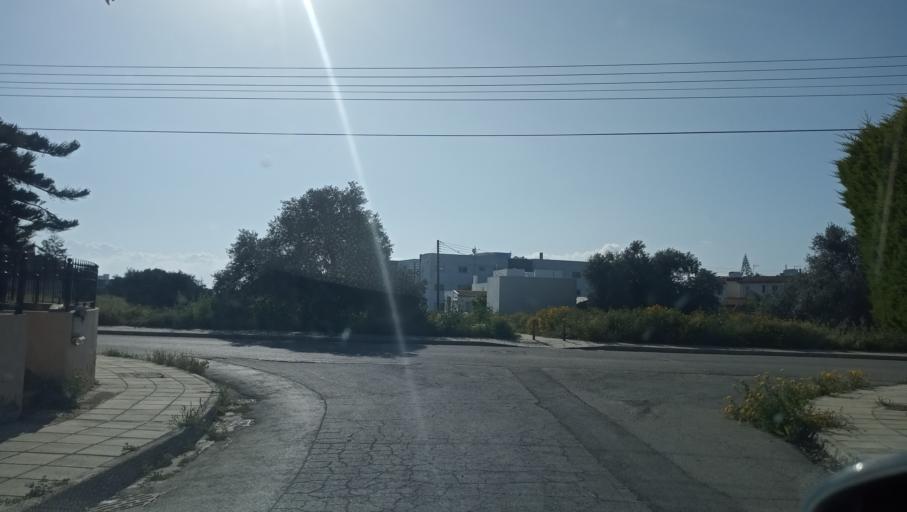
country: CY
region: Lefkosia
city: Tseri
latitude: 35.0692
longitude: 33.3176
